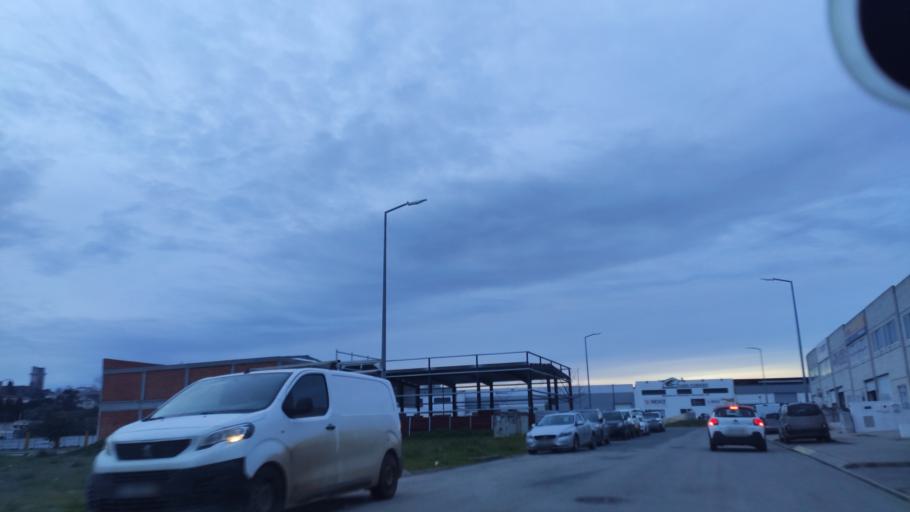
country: PT
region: Beja
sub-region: Beja
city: Beja
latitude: 38.0205
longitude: -7.8530
